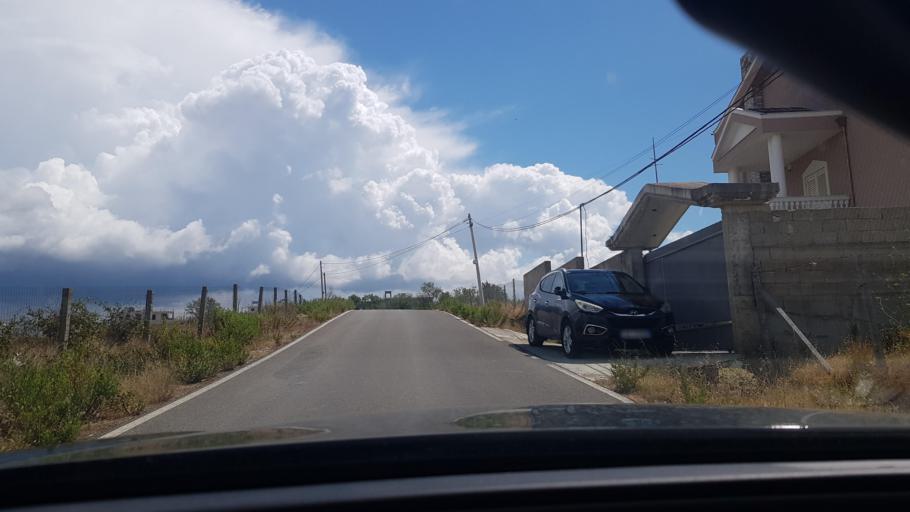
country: AL
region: Durres
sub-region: Rrethi i Durresit
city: Rrashbull
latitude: 41.2927
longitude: 19.5353
